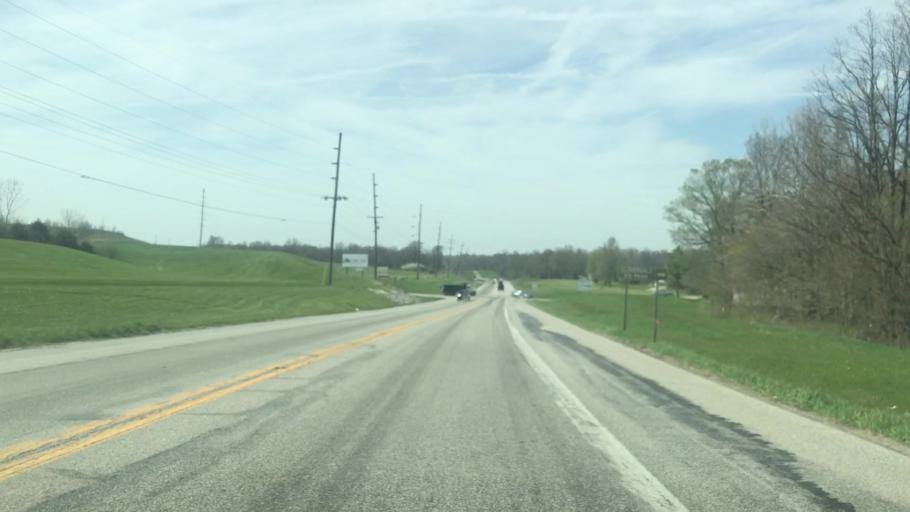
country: US
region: Indiana
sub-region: Putnam County
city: Cloverdale
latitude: 39.5426
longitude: -86.8056
